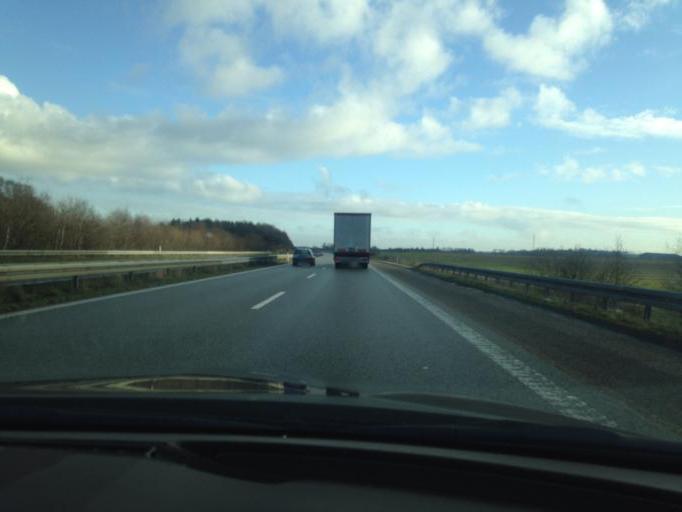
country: DK
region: South Denmark
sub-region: Vejen Kommune
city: Vejen
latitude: 55.4961
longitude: 9.0929
